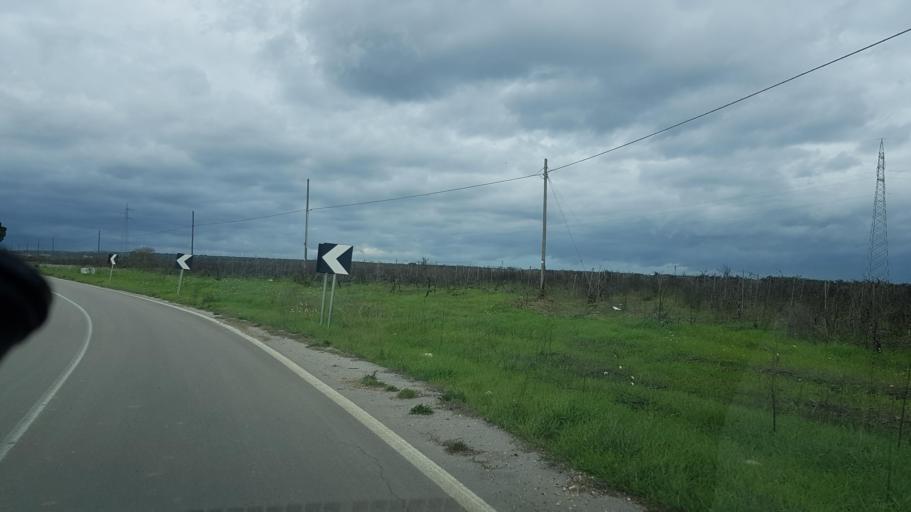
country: IT
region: Apulia
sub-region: Provincia di Brindisi
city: Francavilla Fontana
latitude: 40.5410
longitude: 17.5658
